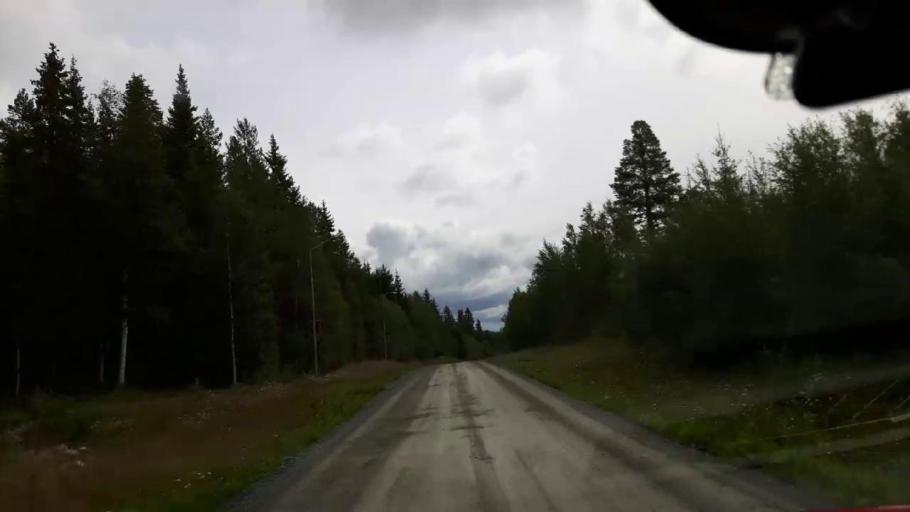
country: SE
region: Jaemtland
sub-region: Krokoms Kommun
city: Valla
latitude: 63.6691
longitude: 13.9590
